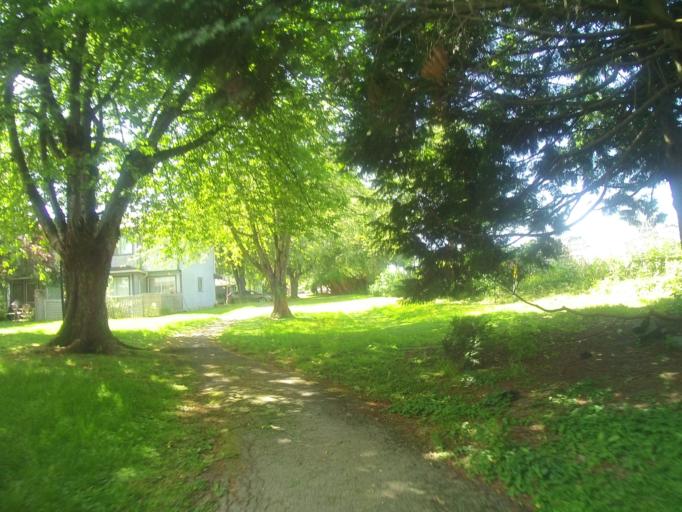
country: CA
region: British Columbia
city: Richmond
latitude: 49.1901
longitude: -123.0897
